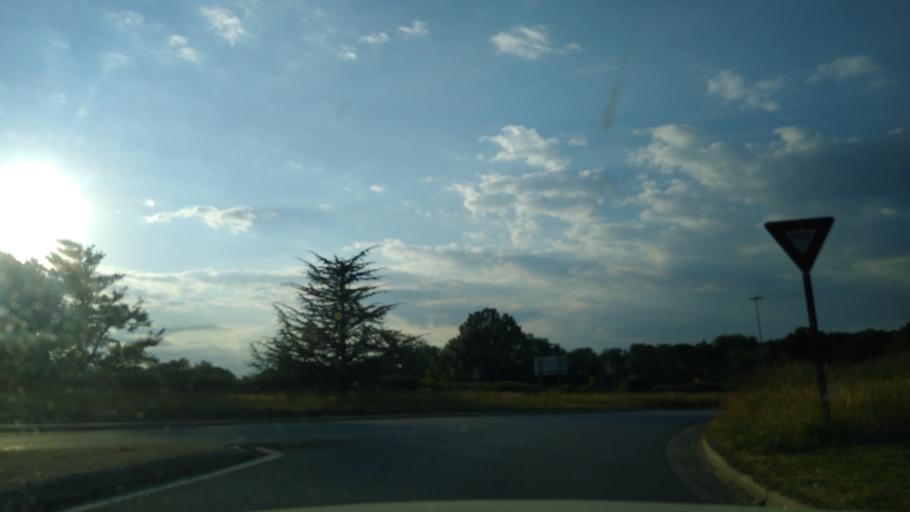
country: US
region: North Carolina
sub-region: Guilford County
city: Greensboro
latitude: 36.1130
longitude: -79.7548
